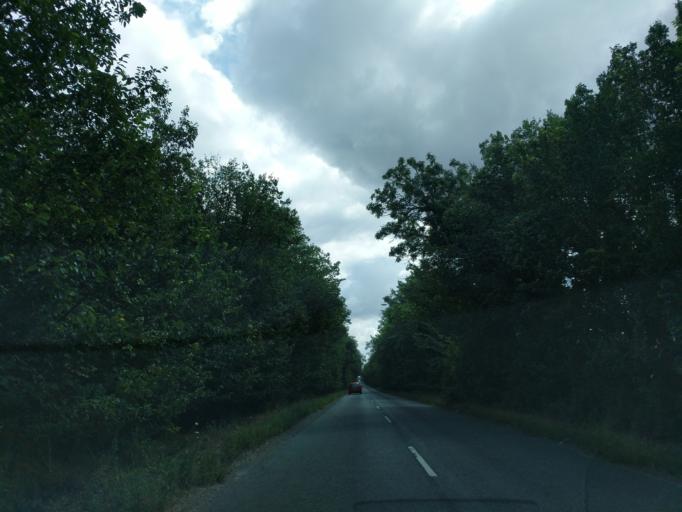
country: GB
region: England
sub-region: Cambridgeshire
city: Isleham
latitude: 52.3106
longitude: 0.4137
